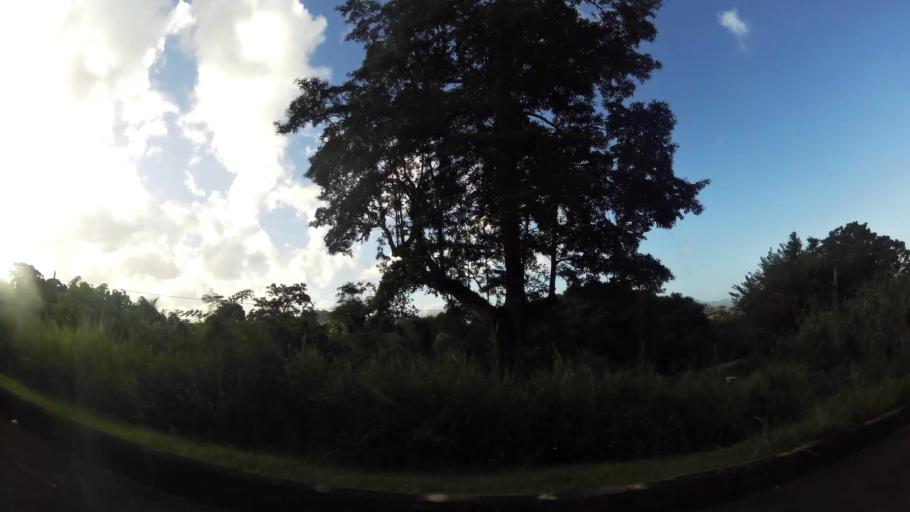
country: MQ
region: Martinique
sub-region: Martinique
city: Ducos
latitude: 14.6025
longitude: -60.9588
